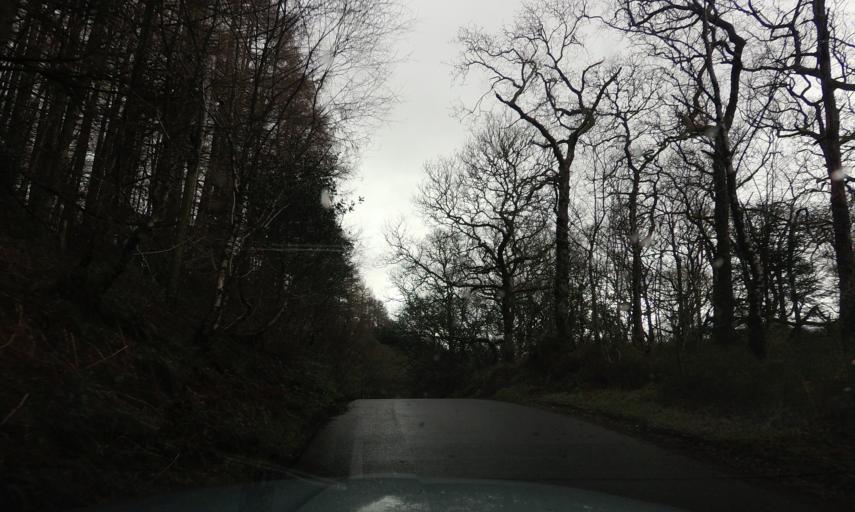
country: GB
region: Scotland
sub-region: West Dunbartonshire
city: Balloch
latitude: 56.1300
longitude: -4.6094
